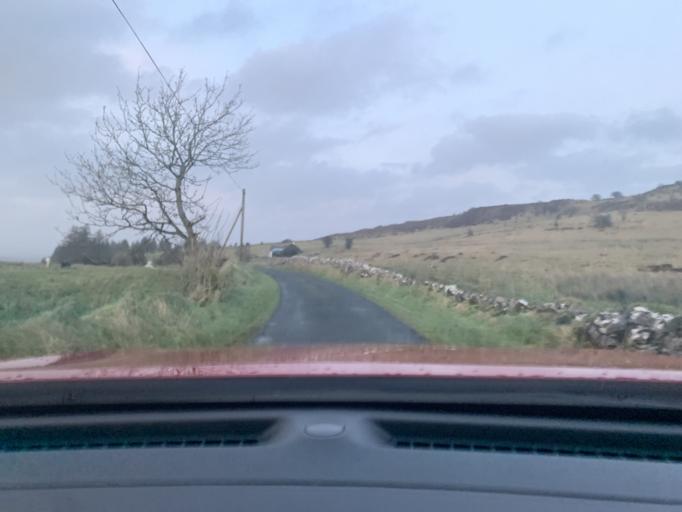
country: IE
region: Connaught
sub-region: Sligo
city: Ballymote
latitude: 54.0523
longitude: -8.3967
